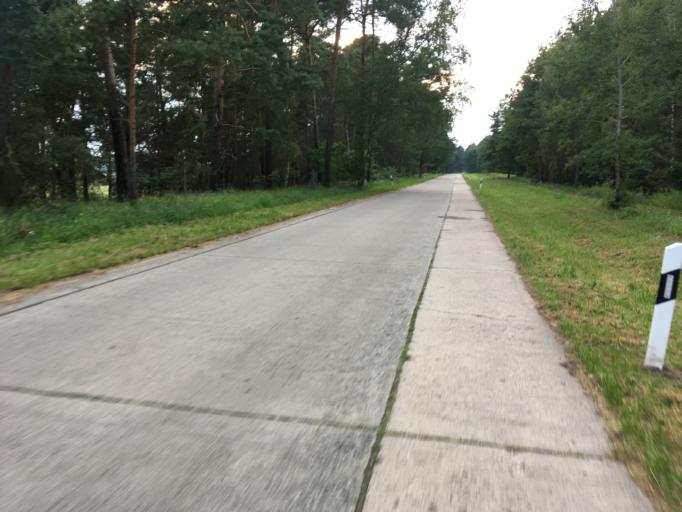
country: DE
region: Brandenburg
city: Grunheide
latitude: 52.3825
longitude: 13.7935
